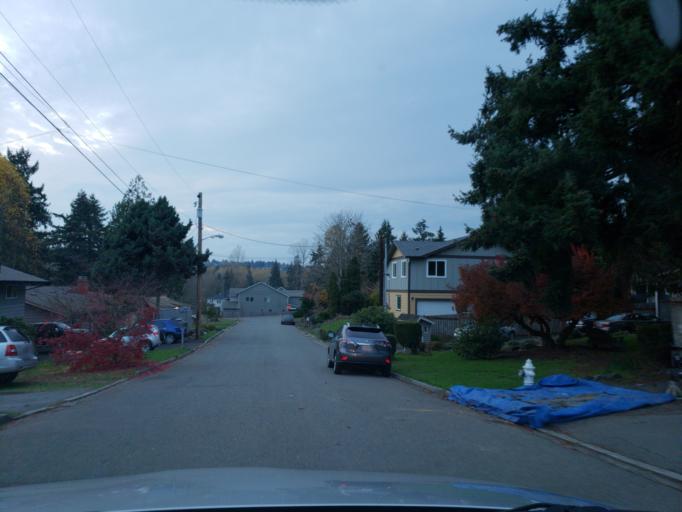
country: US
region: Washington
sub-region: King County
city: Kenmore
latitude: 47.7747
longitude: -122.2392
